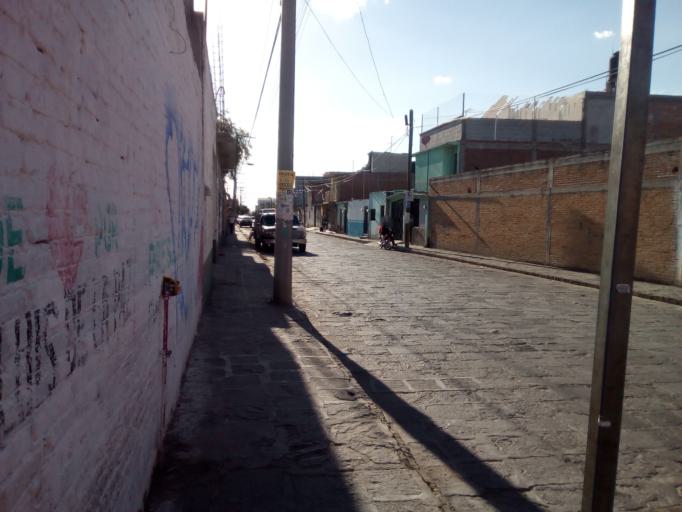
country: MX
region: Guerrero
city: San Luis de la Paz
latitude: 21.2982
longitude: -100.5225
